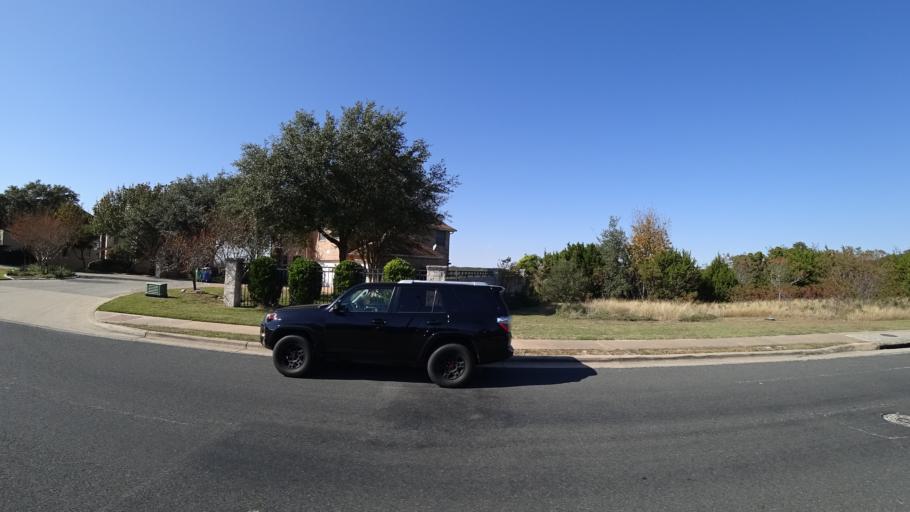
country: US
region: Texas
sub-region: Travis County
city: Lost Creek
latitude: 30.3733
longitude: -97.8566
